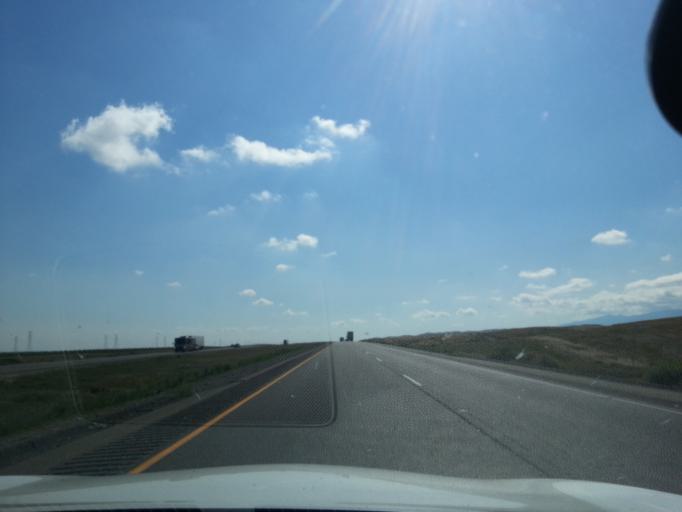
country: US
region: California
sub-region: Fresno County
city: Mendota
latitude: 36.5145
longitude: -120.4685
